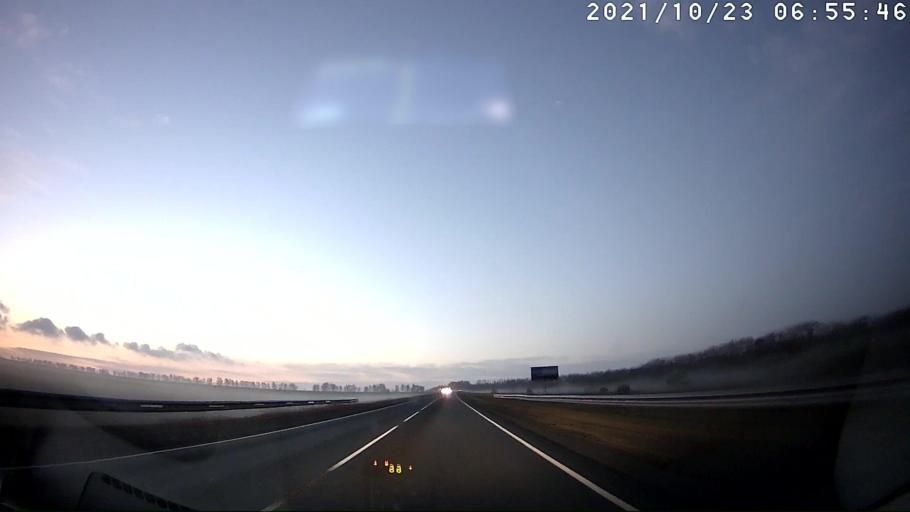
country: RU
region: Saratov
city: Dukhovnitskoye
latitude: 52.7329
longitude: 48.2575
